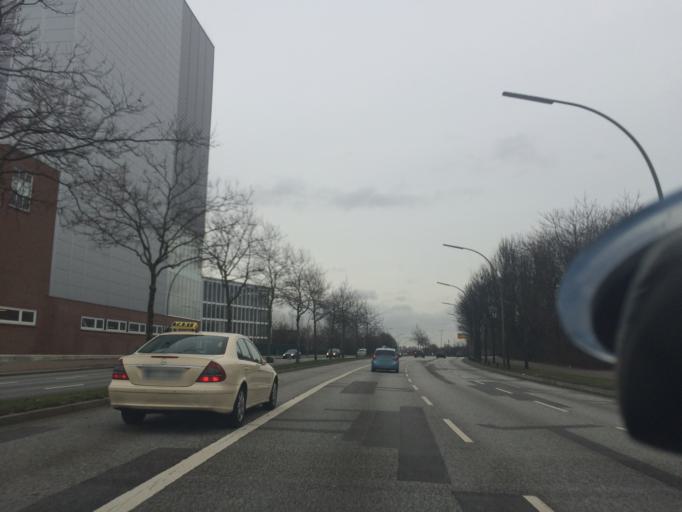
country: DE
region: Hamburg
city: Hammerbrook
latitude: 53.5421
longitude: 10.0277
